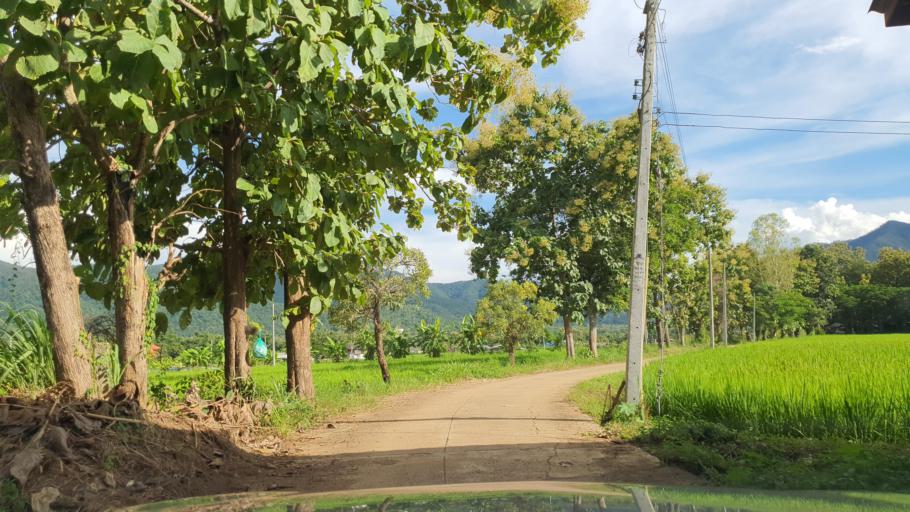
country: TH
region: Chiang Mai
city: Mae On
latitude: 18.7643
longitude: 99.2553
